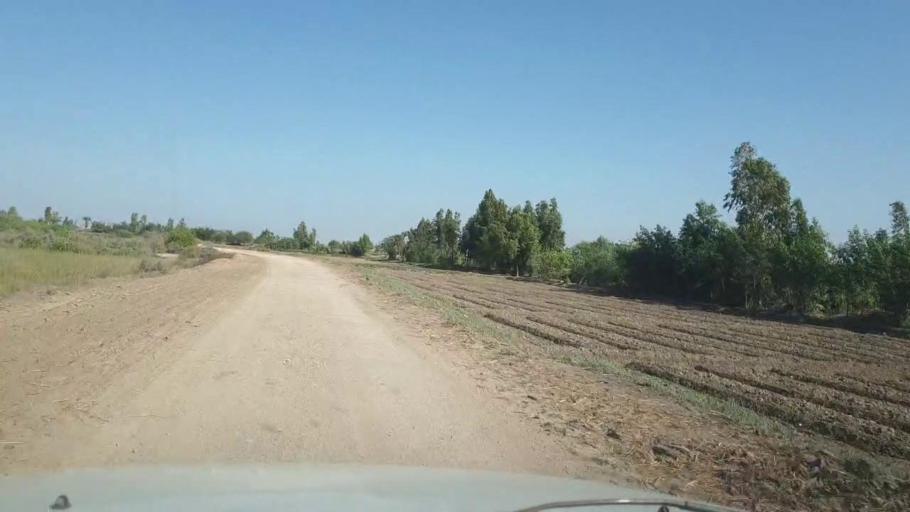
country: PK
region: Sindh
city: Chuhar Jamali
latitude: 24.4841
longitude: 67.8182
